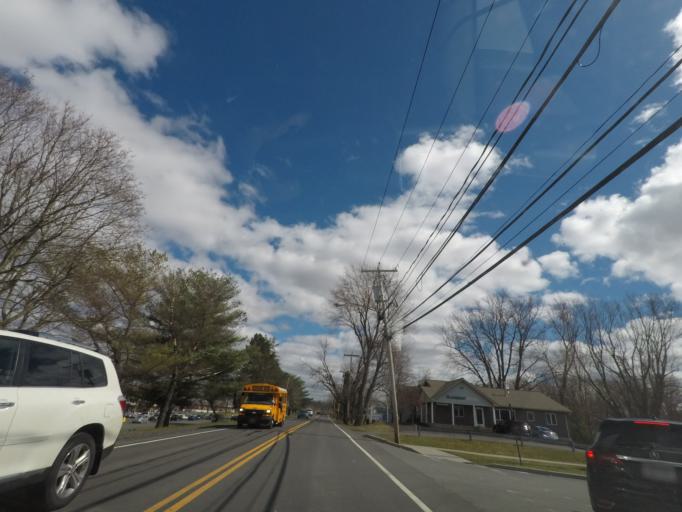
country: US
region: New York
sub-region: Albany County
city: Delmar
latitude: 42.6016
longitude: -73.7911
